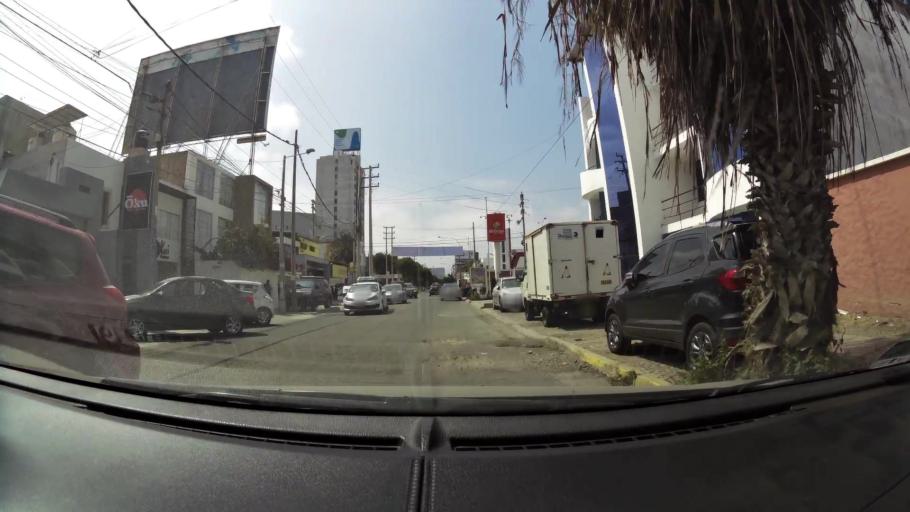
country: PE
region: La Libertad
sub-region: Provincia de Trujillo
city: Buenos Aires
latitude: -8.1300
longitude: -79.0372
